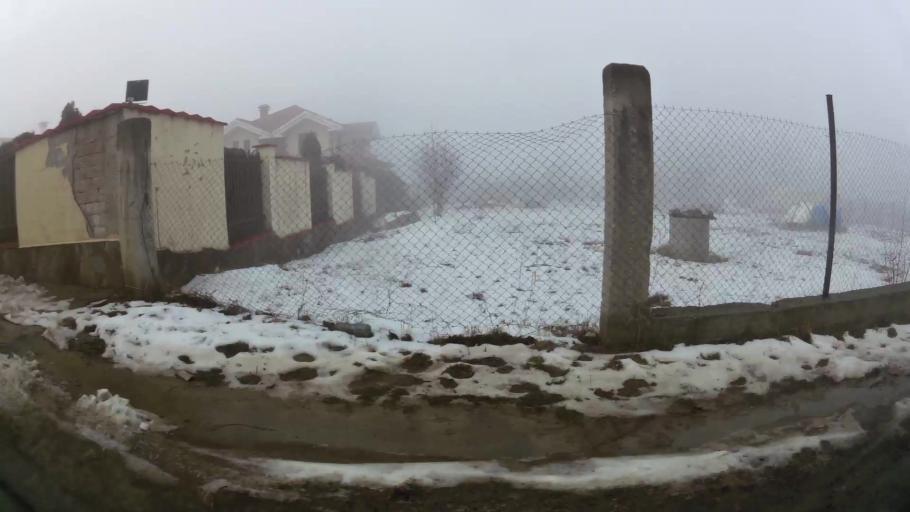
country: BG
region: Sofia-Capital
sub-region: Stolichna Obshtina
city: Sofia
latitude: 42.6558
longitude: 23.2607
